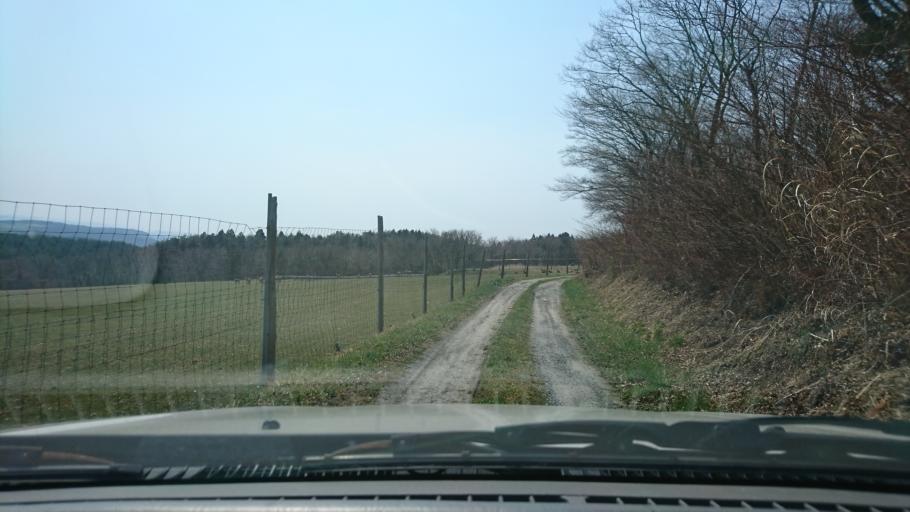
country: JP
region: Iwate
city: Ichinoseki
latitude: 38.8185
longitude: 141.2634
